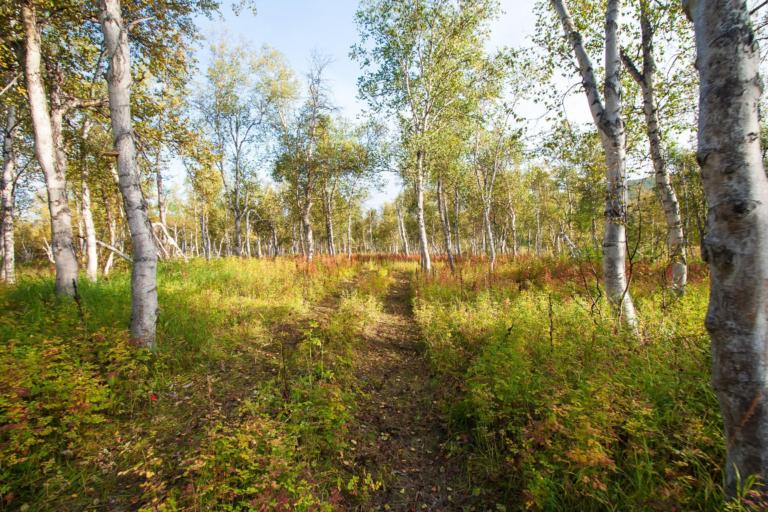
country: RU
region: Kamtsjatka
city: Yelizovo
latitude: 53.7557
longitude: 158.6263
